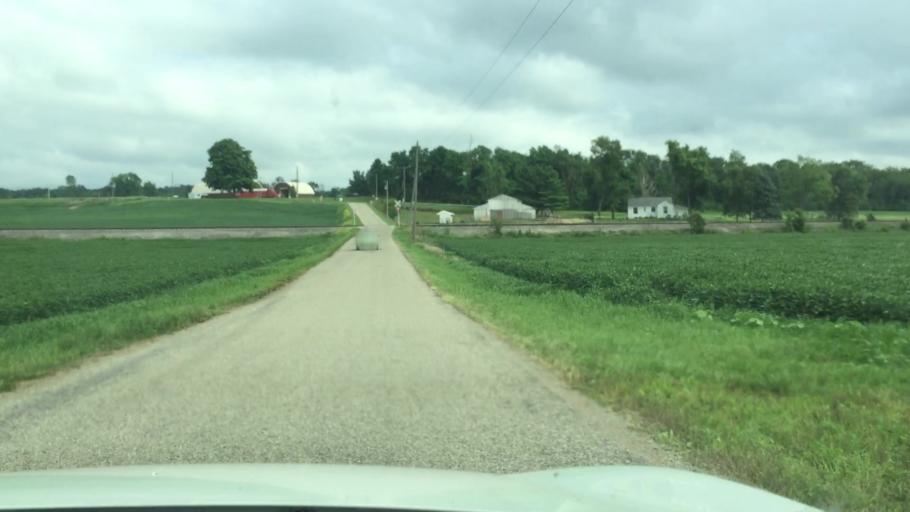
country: US
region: Ohio
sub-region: Champaign County
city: Mechanicsburg
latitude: 40.0483
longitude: -83.6336
